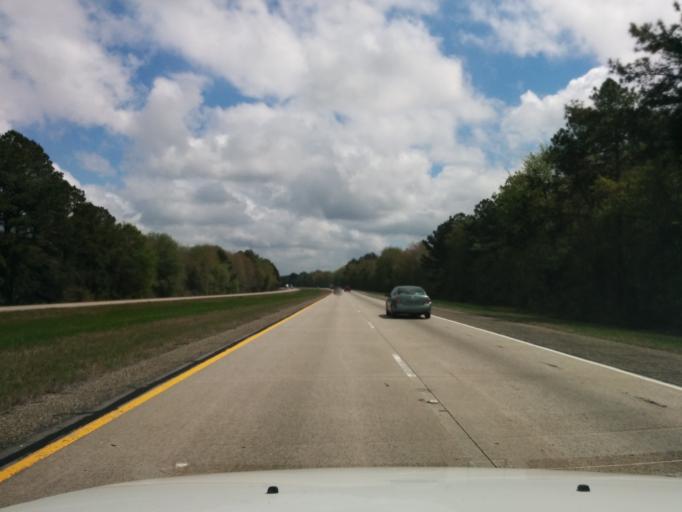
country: US
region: Georgia
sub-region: Bryan County
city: Pembroke
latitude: 32.2326
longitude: -81.6521
